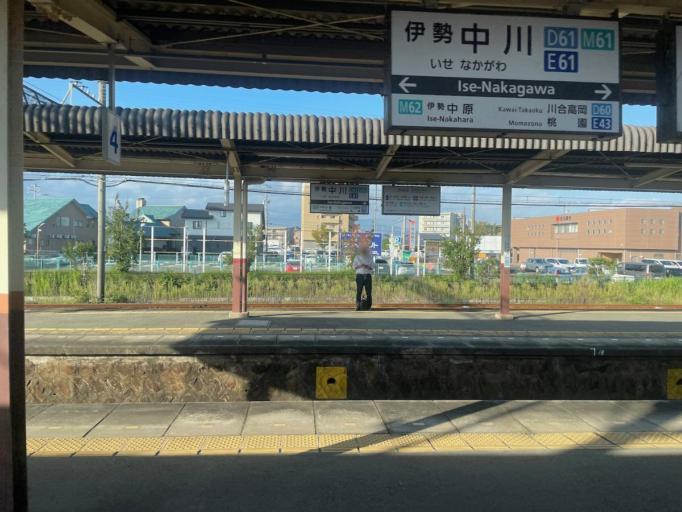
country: JP
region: Mie
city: Hisai-motomachi
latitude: 34.6163
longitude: 136.4971
